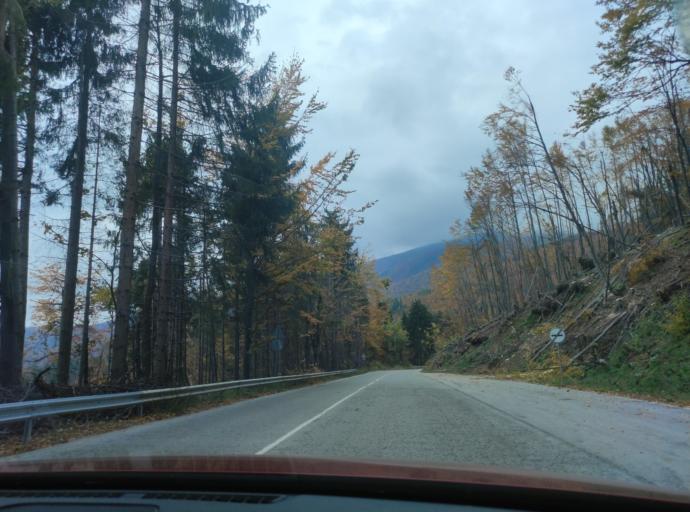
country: BG
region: Montana
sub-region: Obshtina Berkovitsa
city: Berkovitsa
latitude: 43.1476
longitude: 23.1463
